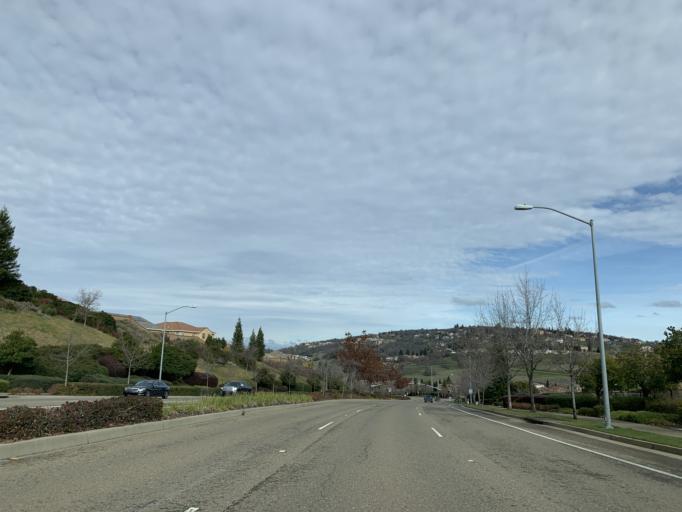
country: US
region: California
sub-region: El Dorado County
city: El Dorado Hills
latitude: 38.6498
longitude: -121.0925
